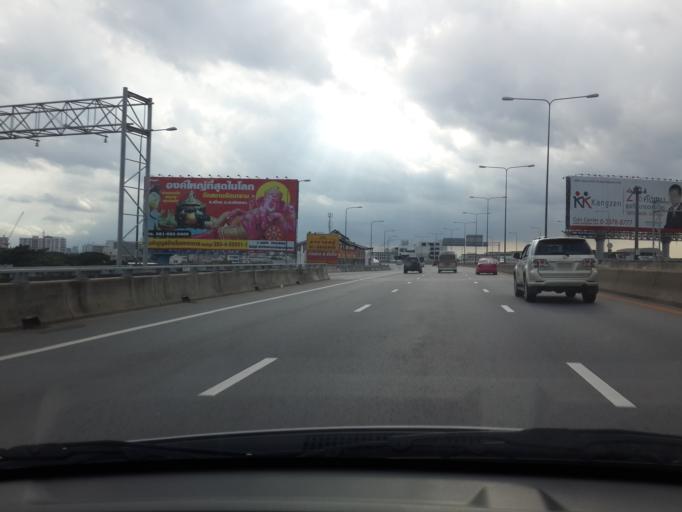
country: TH
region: Bangkok
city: Suan Luang
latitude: 13.7423
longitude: 100.6374
